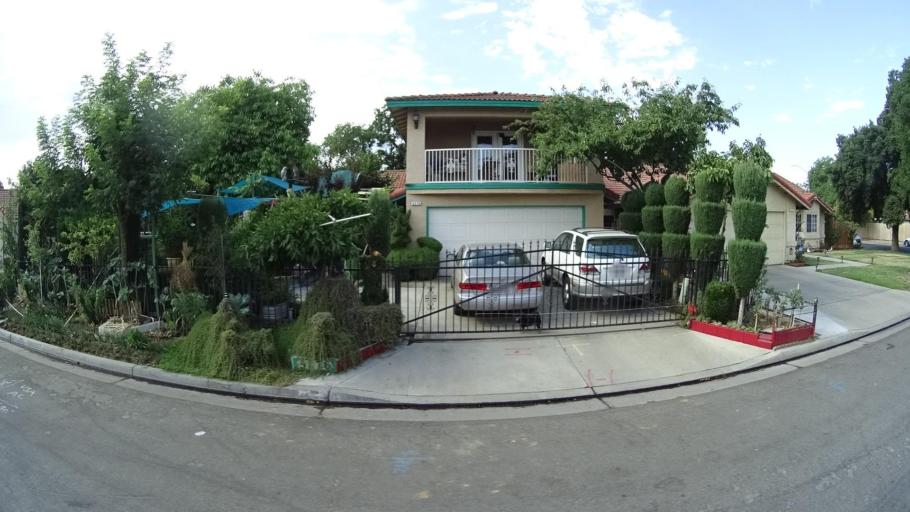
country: US
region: California
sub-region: Fresno County
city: Sunnyside
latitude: 36.7580
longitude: -119.7148
